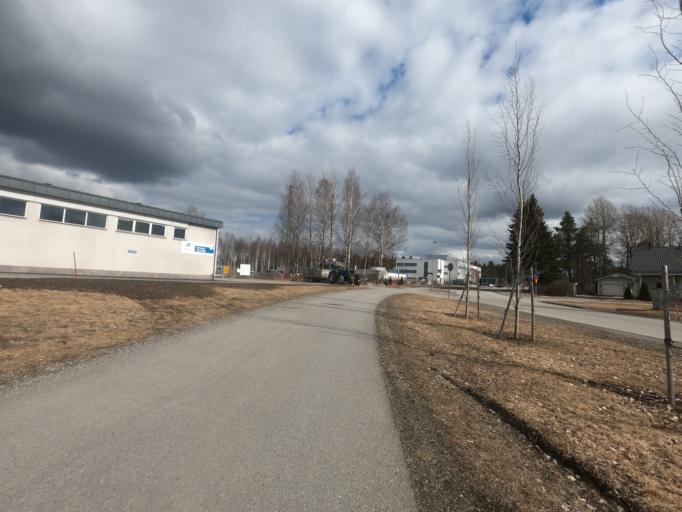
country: FI
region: North Karelia
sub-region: Joensuu
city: Joensuu
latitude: 62.6030
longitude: 29.7848
